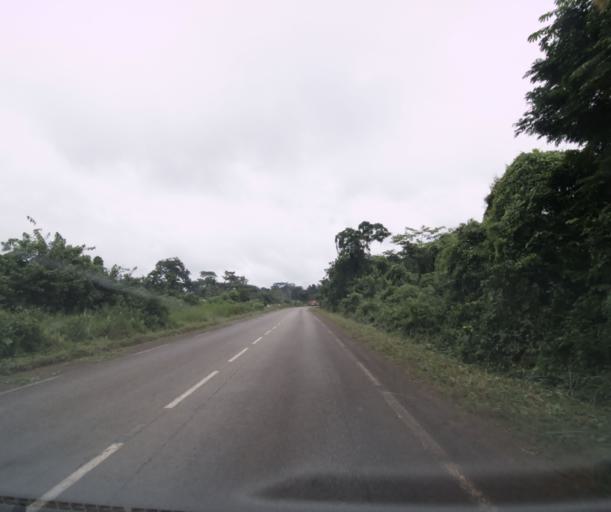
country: CM
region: Littoral
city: Edea
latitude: 3.8256
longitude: 10.3873
